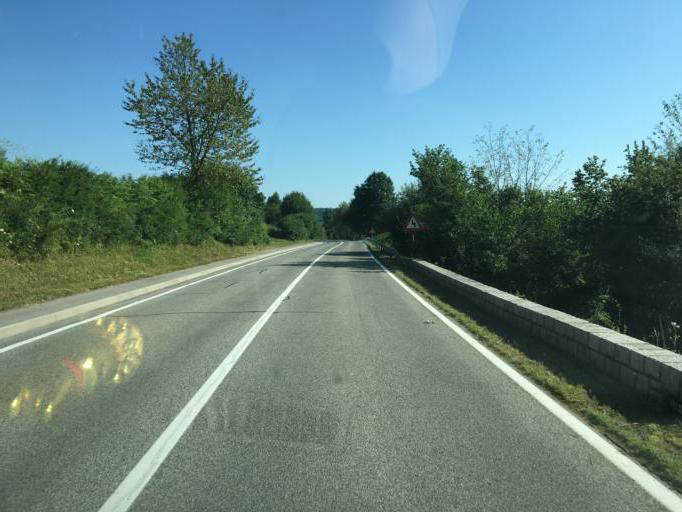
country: HR
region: Licko-Senjska
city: Jezerce
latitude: 45.0018
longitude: 15.6519
